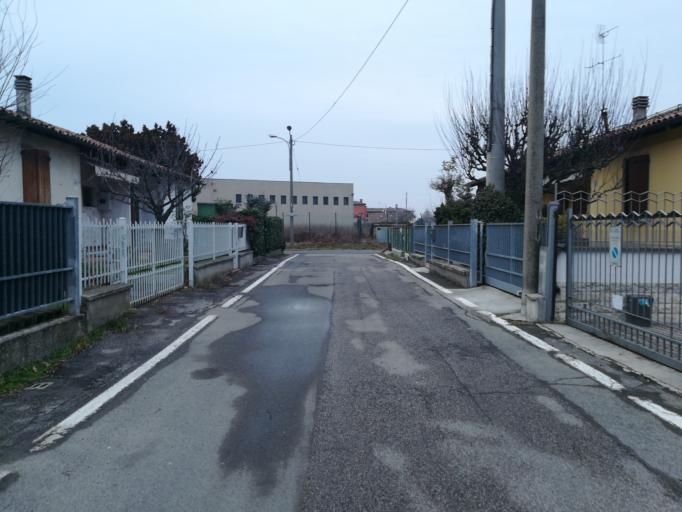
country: IT
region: Emilia-Romagna
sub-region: Provincia di Bologna
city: Progresso
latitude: 44.5489
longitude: 11.3516
